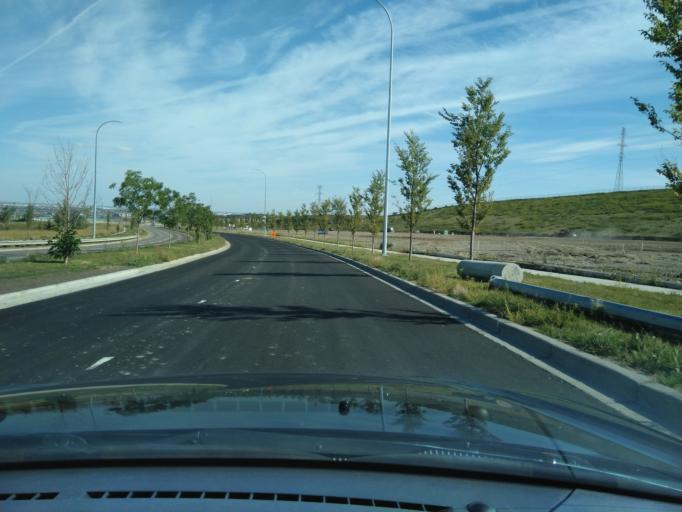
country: CA
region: Alberta
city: Calgary
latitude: 51.1711
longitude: -114.1733
